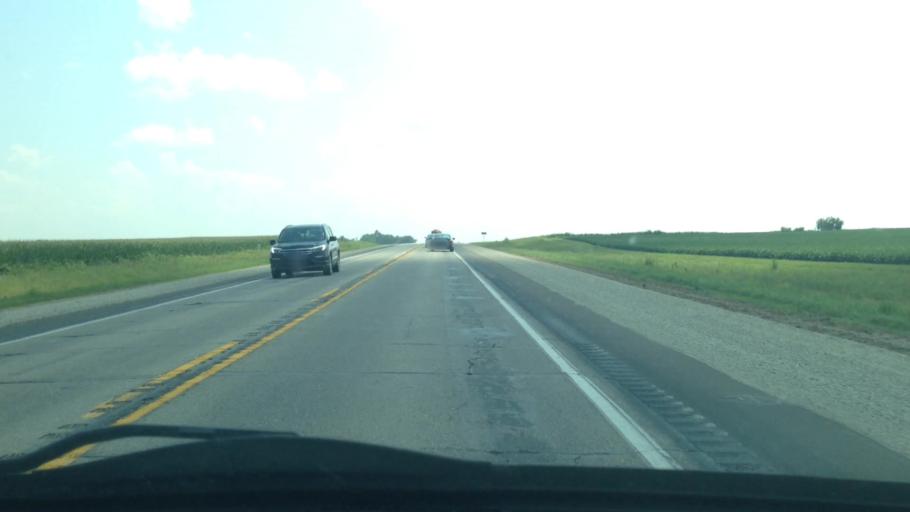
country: US
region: Iowa
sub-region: Howard County
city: Cresco
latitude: 43.4314
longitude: -92.2986
